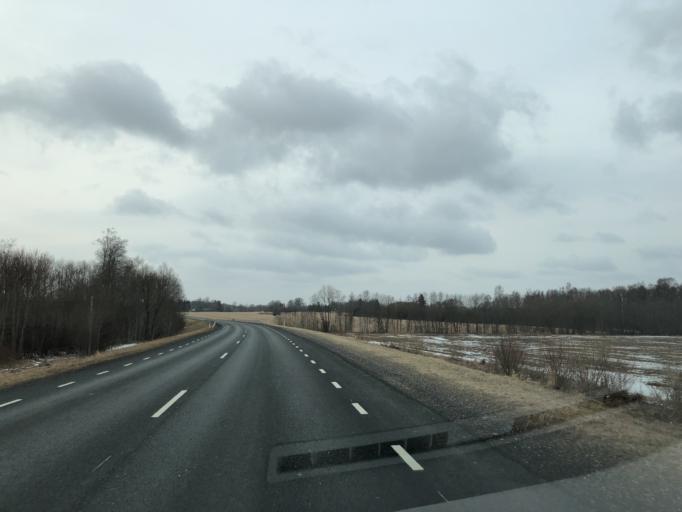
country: EE
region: Viljandimaa
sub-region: Suure-Jaani vald
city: Suure-Jaani
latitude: 58.5589
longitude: 25.4408
